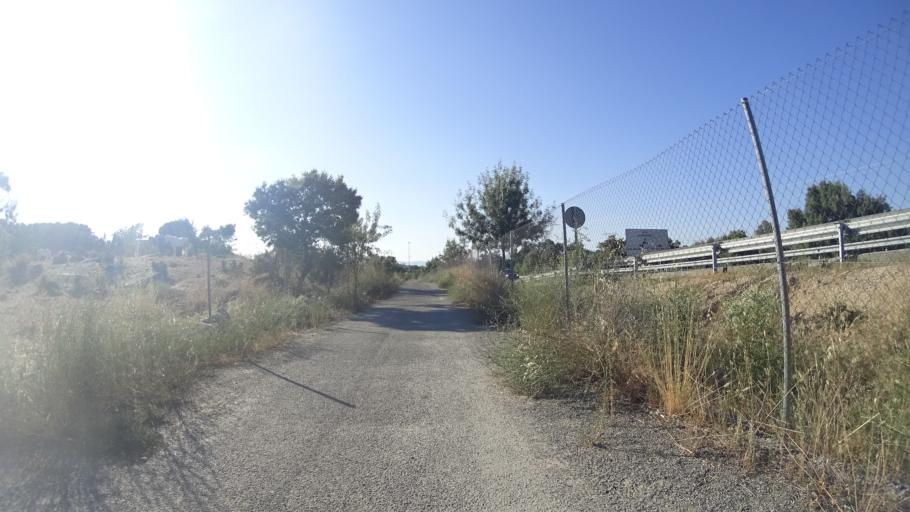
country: ES
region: Madrid
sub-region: Provincia de Madrid
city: Galapagar
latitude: 40.5763
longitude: -3.9887
